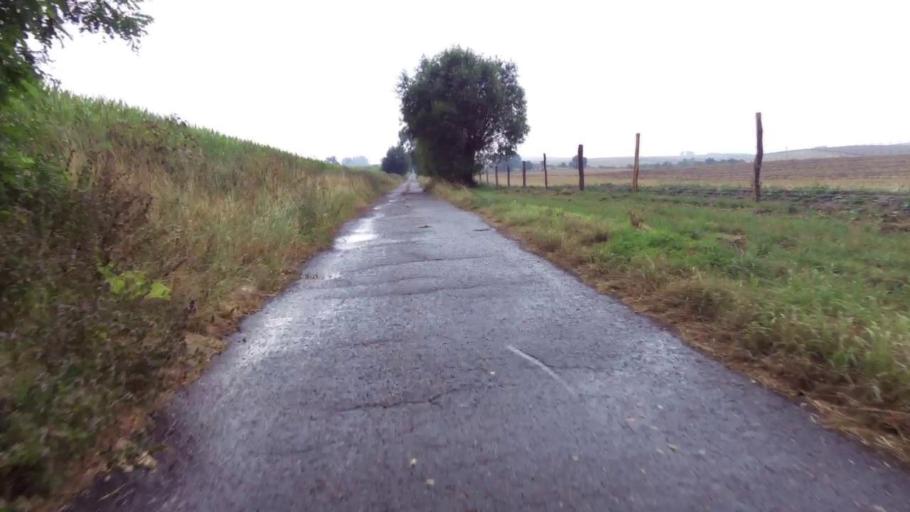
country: PL
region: West Pomeranian Voivodeship
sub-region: Powiat choszczenski
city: Recz
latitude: 53.2624
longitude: 15.4613
